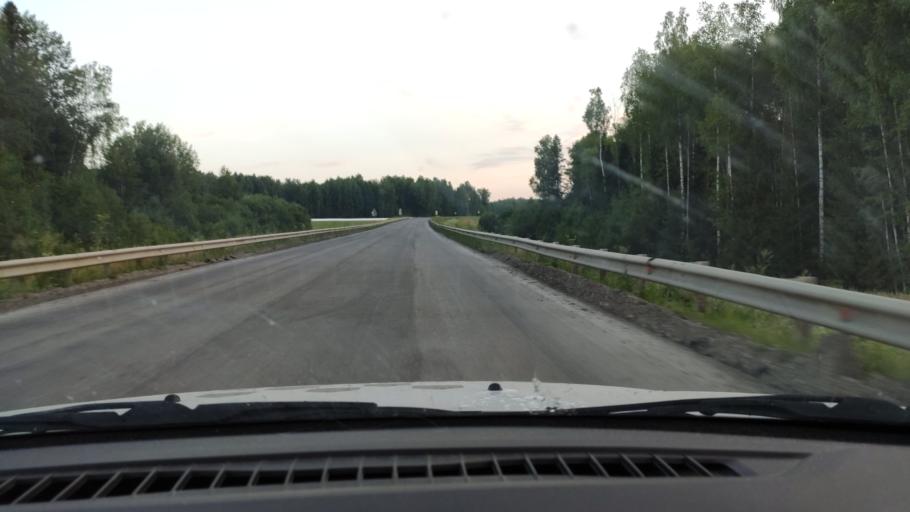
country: RU
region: Perm
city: Siva
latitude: 58.4593
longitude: 54.4094
